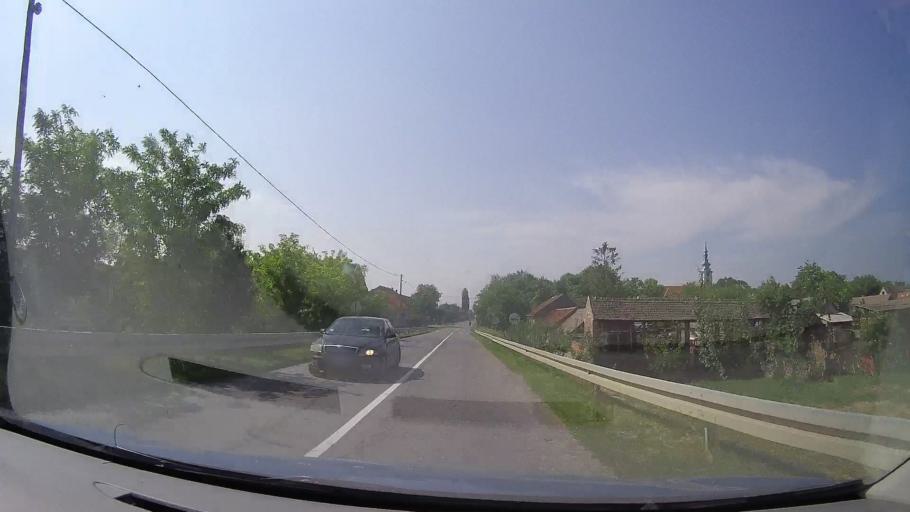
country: RS
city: Jarkovac
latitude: 45.2725
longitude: 20.7645
